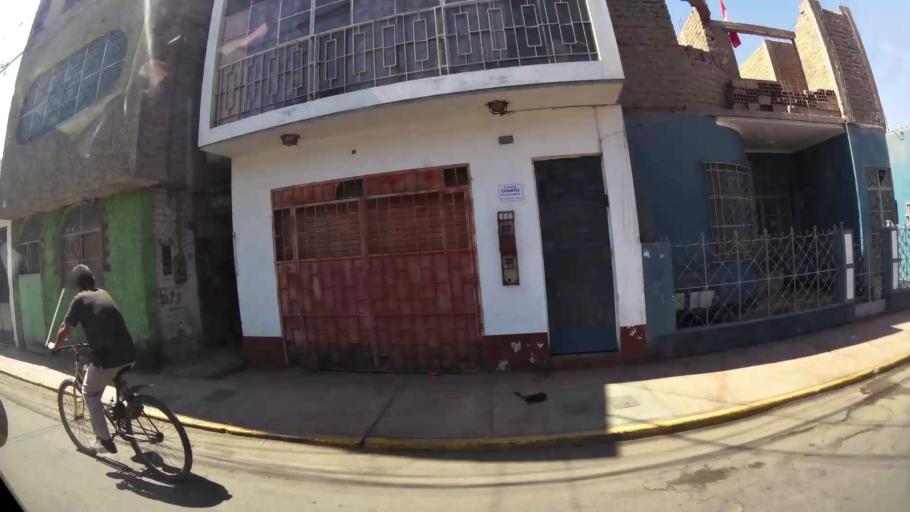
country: PE
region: Ica
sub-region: Provincia de Ica
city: Ica
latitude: -14.0662
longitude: -75.7252
